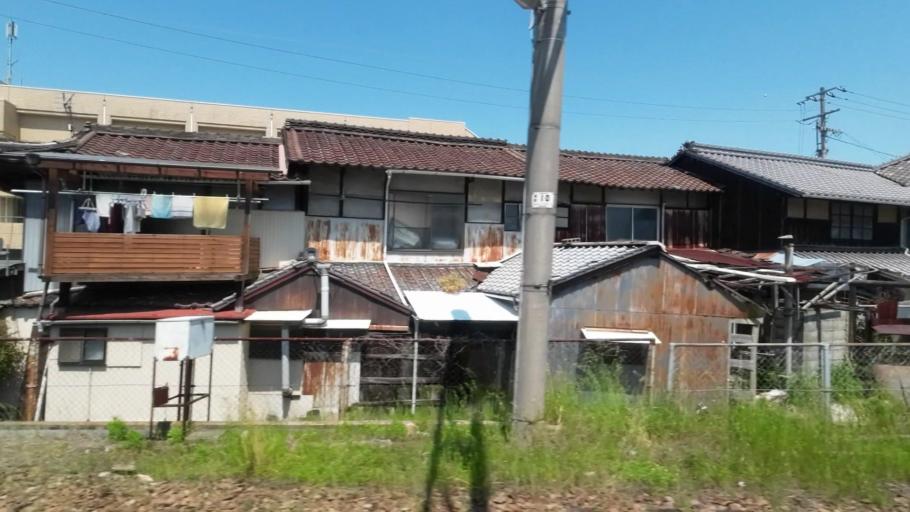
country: JP
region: Ehime
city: Hojo
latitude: 34.0338
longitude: 132.8425
